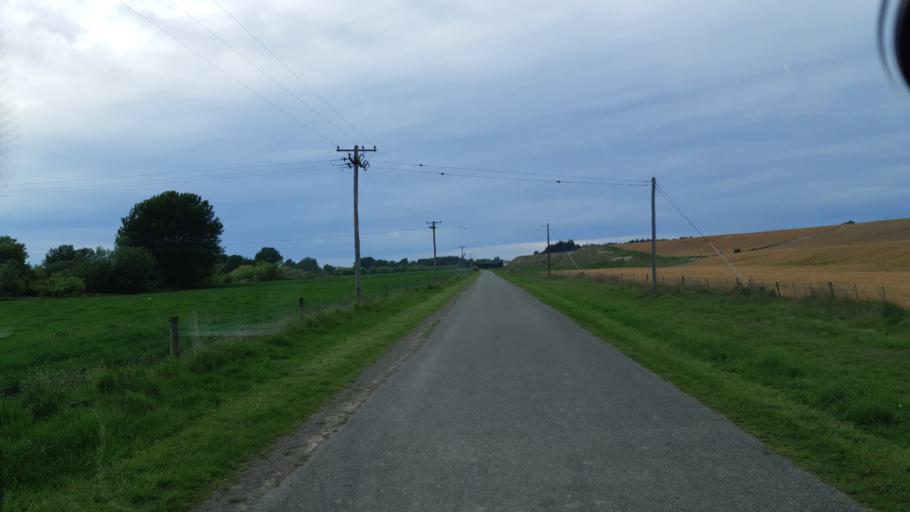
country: NZ
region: Canterbury
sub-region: Timaru District
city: Timaru
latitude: -44.5391
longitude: 171.1525
